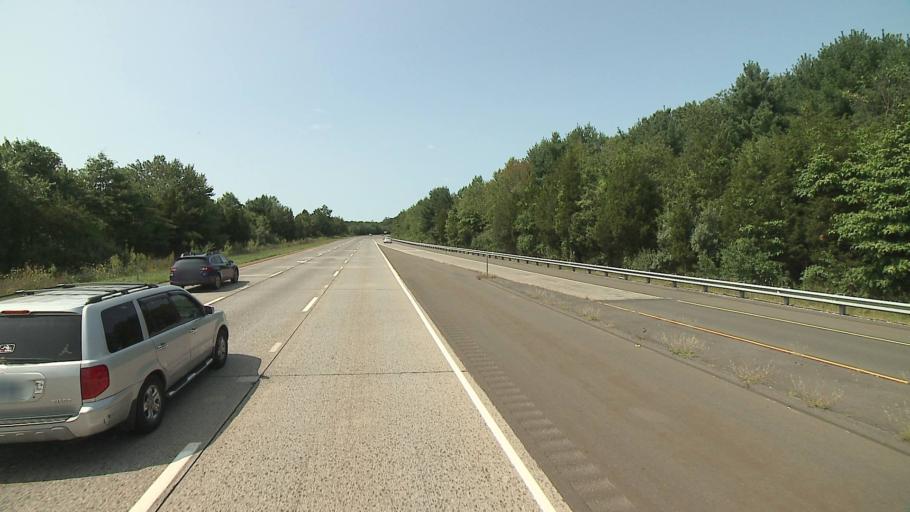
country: US
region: Connecticut
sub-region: Fairfield County
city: Trumbull
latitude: 41.2544
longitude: -73.2006
